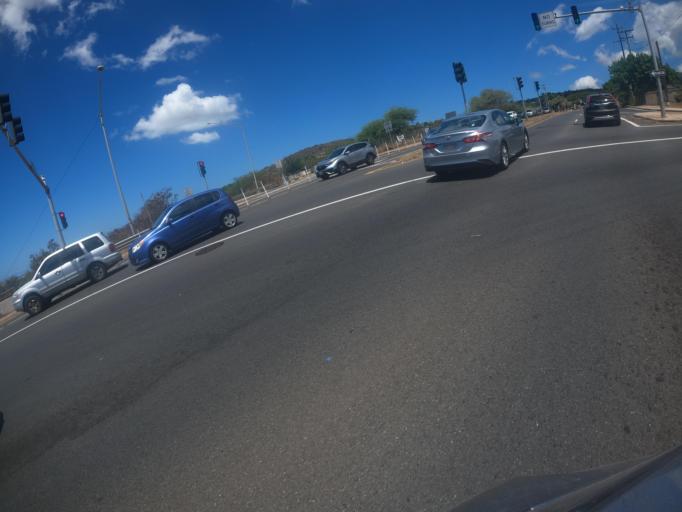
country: US
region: Hawaii
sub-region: Honolulu County
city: Makakilo City
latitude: 21.3427
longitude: -158.0782
